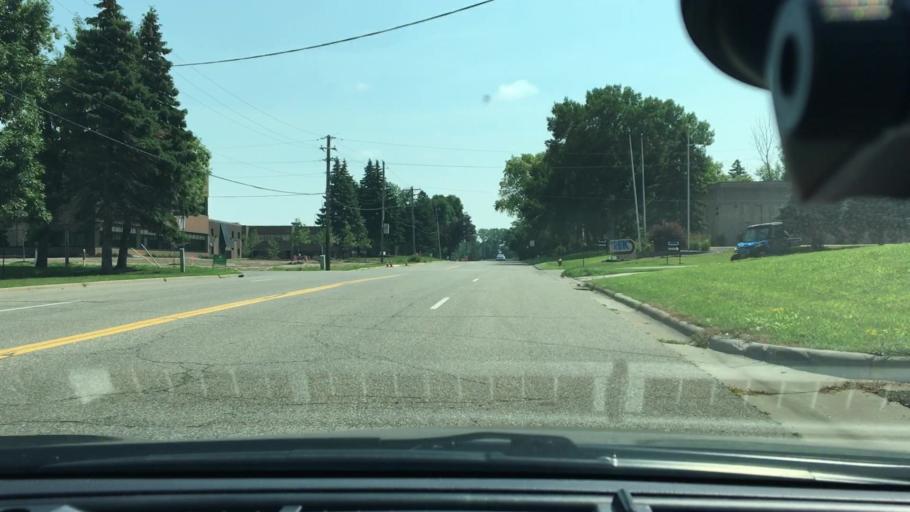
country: US
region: Minnesota
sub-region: Hennepin County
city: New Hope
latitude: 44.9894
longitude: -93.4062
